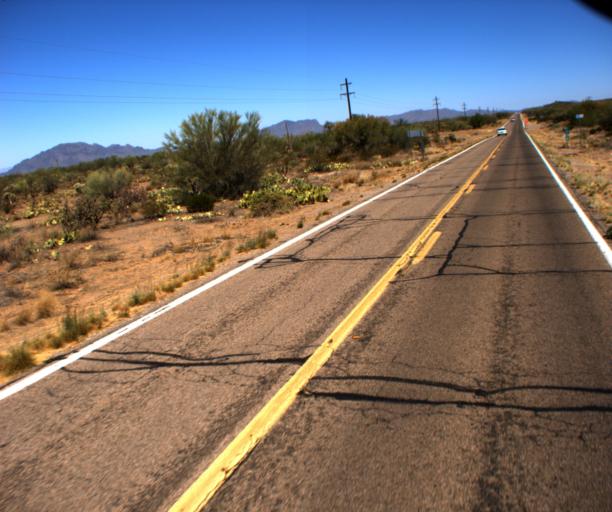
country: US
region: Arizona
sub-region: Pima County
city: Sells
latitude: 31.9708
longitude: -111.9598
